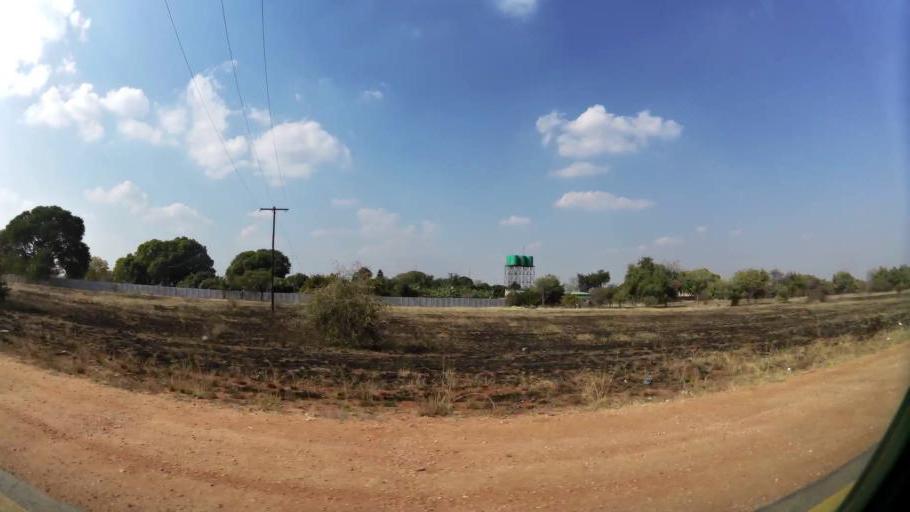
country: ZA
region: North-West
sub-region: Bojanala Platinum District Municipality
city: Rustenburg
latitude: -25.4895
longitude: 27.0858
